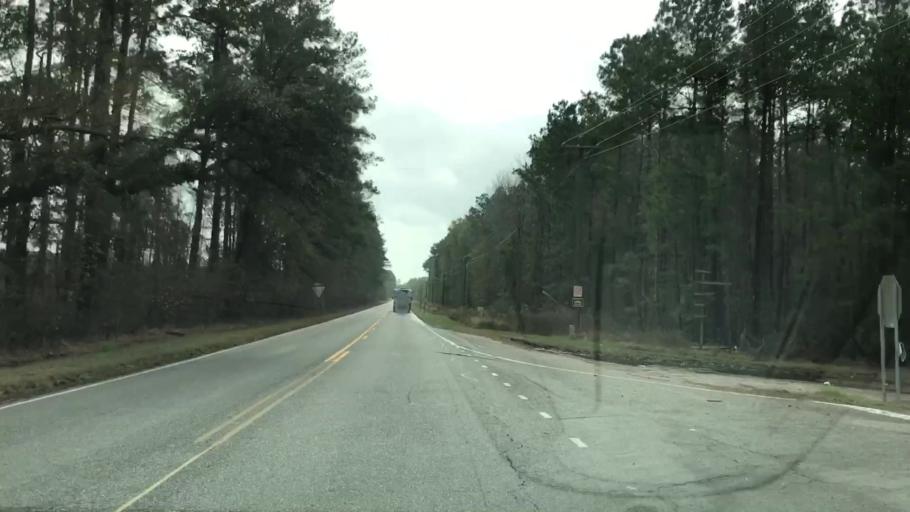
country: US
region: South Carolina
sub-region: Georgetown County
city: Murrells Inlet
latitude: 33.6315
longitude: -79.1881
